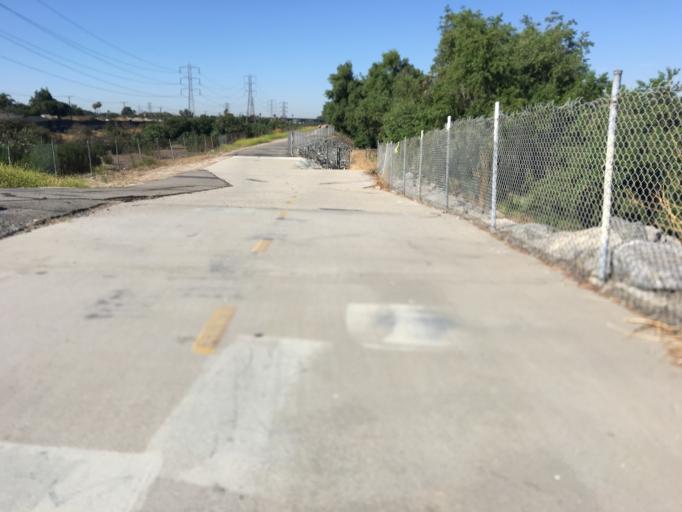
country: US
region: California
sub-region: Los Angeles County
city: West Whittier-Los Nietos
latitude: 33.9750
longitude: -118.0829
